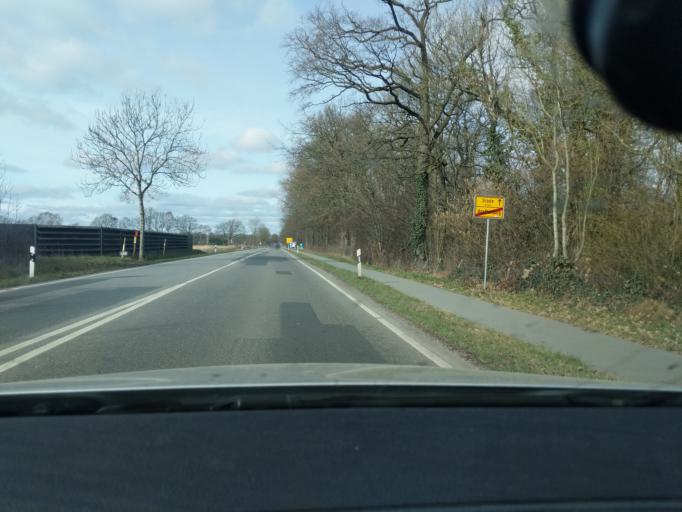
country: DE
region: Lower Saxony
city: Agathenburg
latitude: 53.5666
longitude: 9.5251
